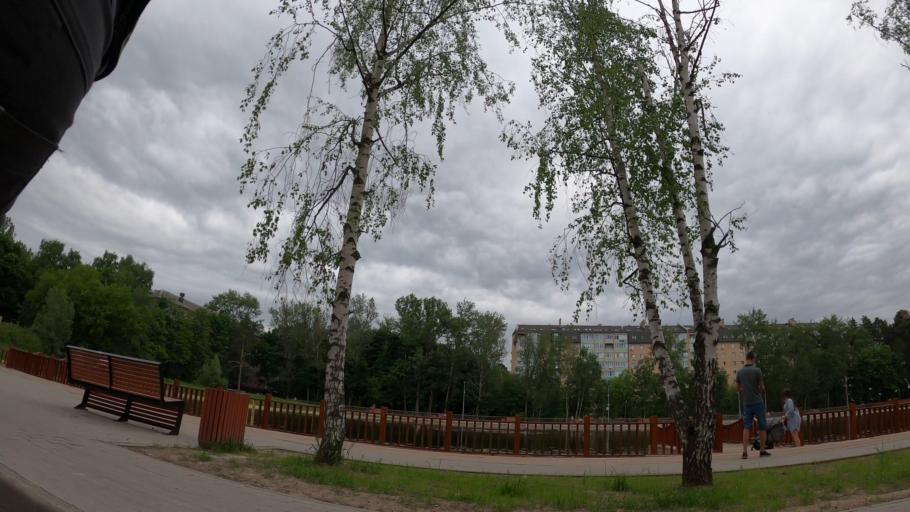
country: RU
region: Moskovskaya
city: Yubileyny
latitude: 55.9410
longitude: 37.8363
